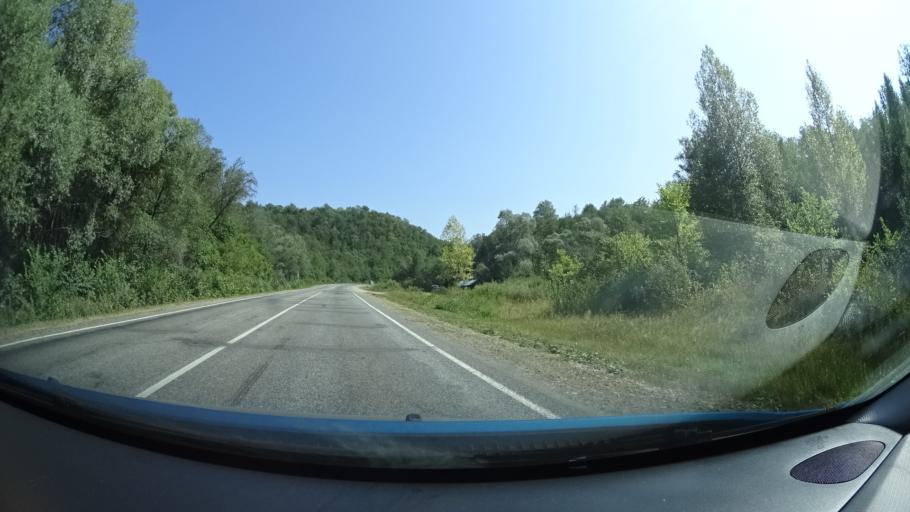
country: RU
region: Bashkortostan
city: Inzer
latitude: 54.3395
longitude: 57.0860
